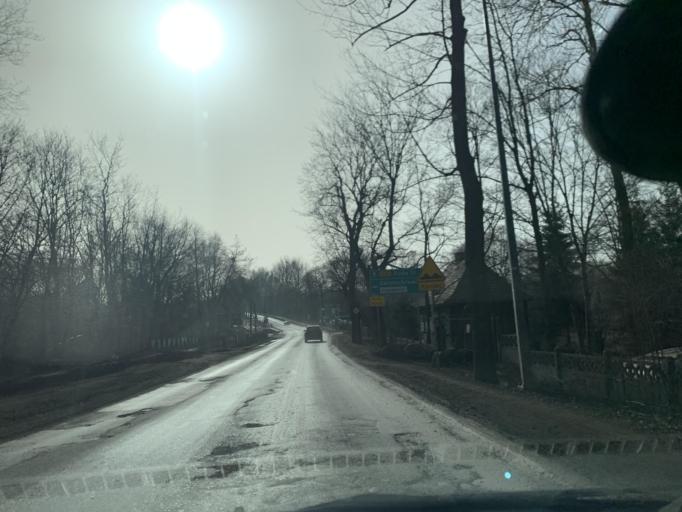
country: PL
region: Silesian Voivodeship
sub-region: Swietochlowice
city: Swietochlowice
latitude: 50.3285
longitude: 18.8942
